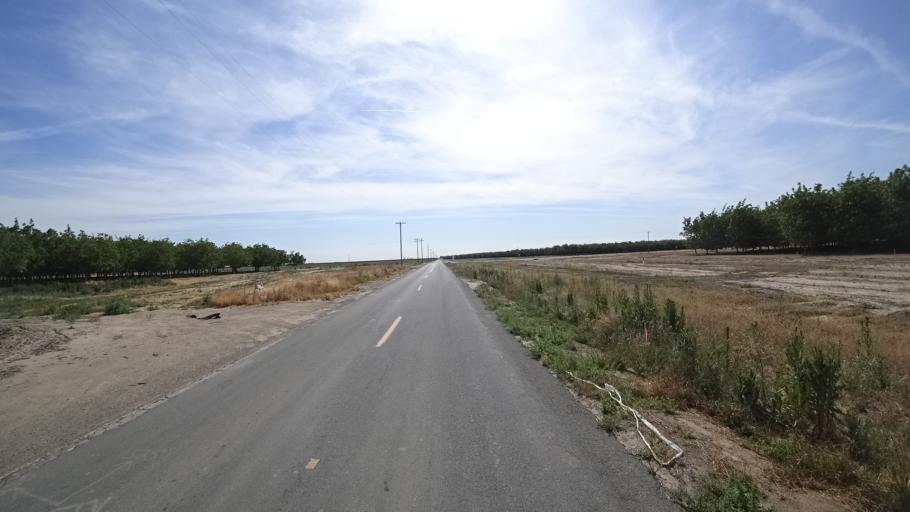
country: US
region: California
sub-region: Kings County
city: Lucerne
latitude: 36.4158
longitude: -119.6029
